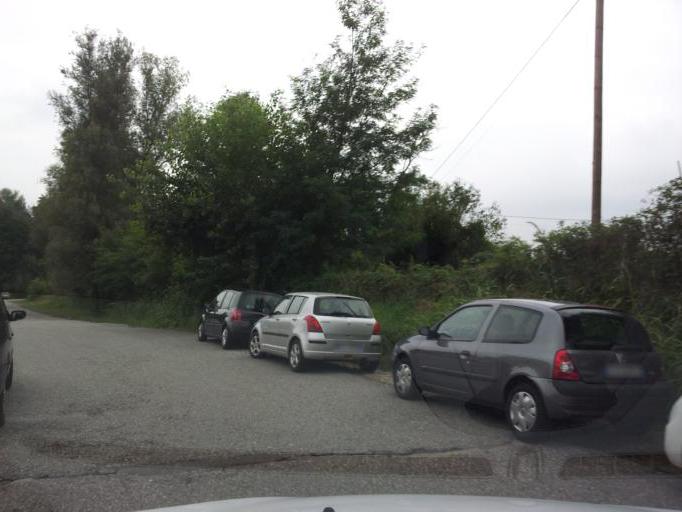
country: IT
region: Lombardy
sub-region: Provincia di Varese
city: Sesto Calende
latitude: 45.7314
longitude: 8.6238
